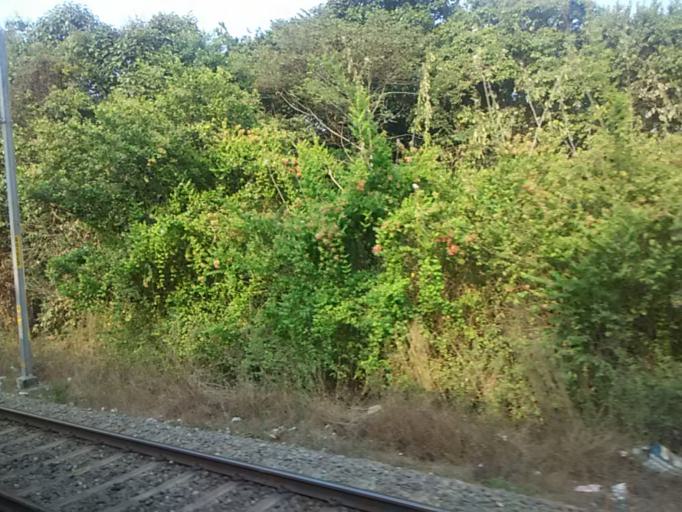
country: IN
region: Kerala
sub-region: Malappuram
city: Pariyapuram
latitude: 11.0664
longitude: 75.8556
